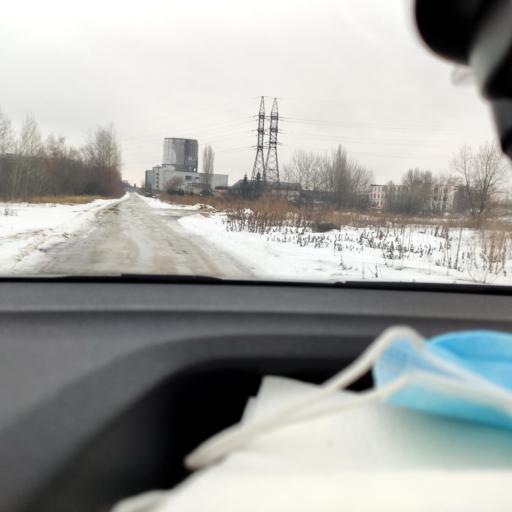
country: RU
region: Voronezj
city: Shilovo
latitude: 51.5646
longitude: 39.1416
